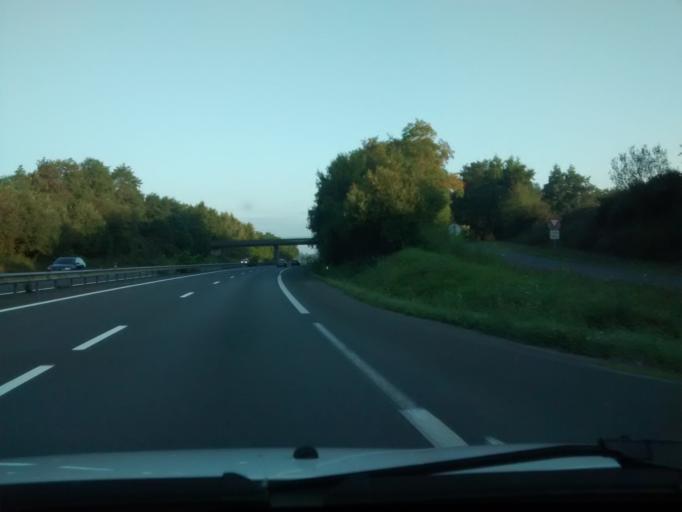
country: FR
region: Brittany
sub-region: Departement des Cotes-d'Armor
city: Broons
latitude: 48.3420
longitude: -2.2862
